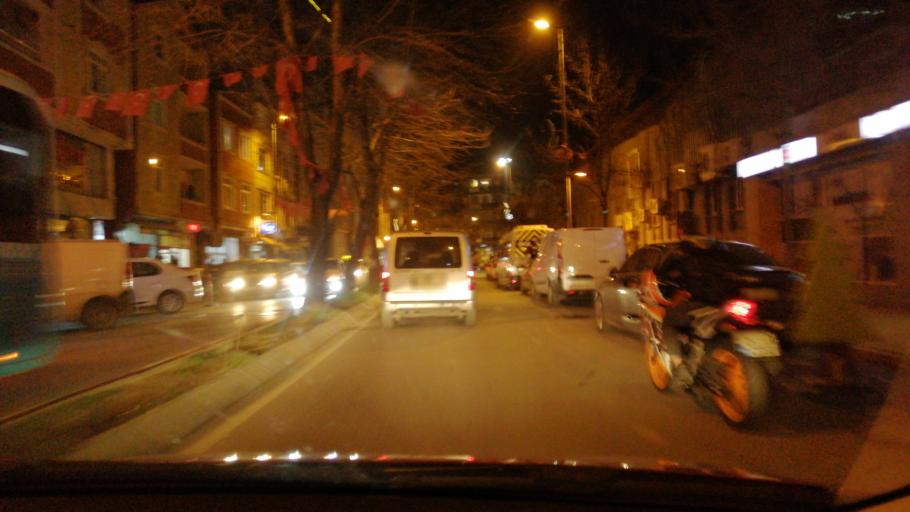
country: TR
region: Istanbul
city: Sisli
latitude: 41.0832
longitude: 28.9734
